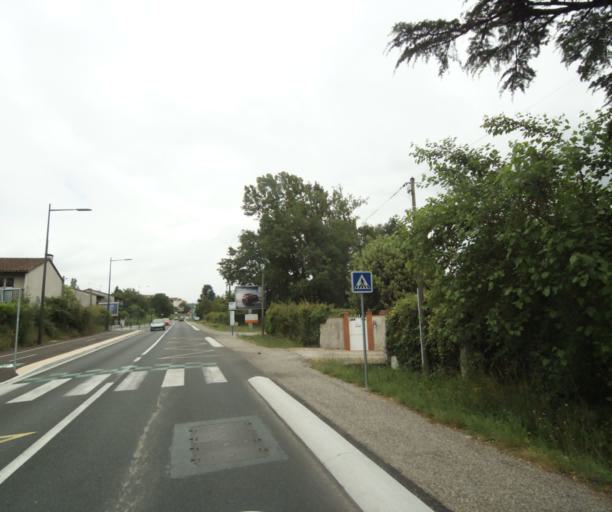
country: FR
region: Midi-Pyrenees
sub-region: Departement du Tarn-et-Garonne
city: Montauban
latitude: 44.0039
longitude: 1.3631
